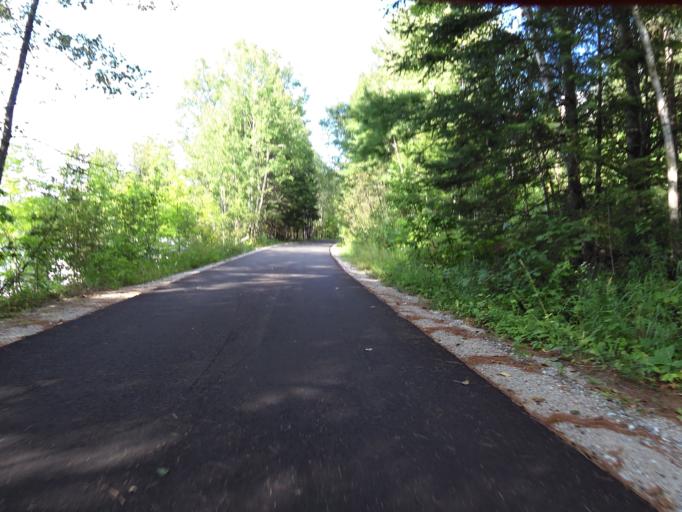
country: CA
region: Quebec
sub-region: Outaouais
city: Maniwaki
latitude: 46.2072
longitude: -76.0408
